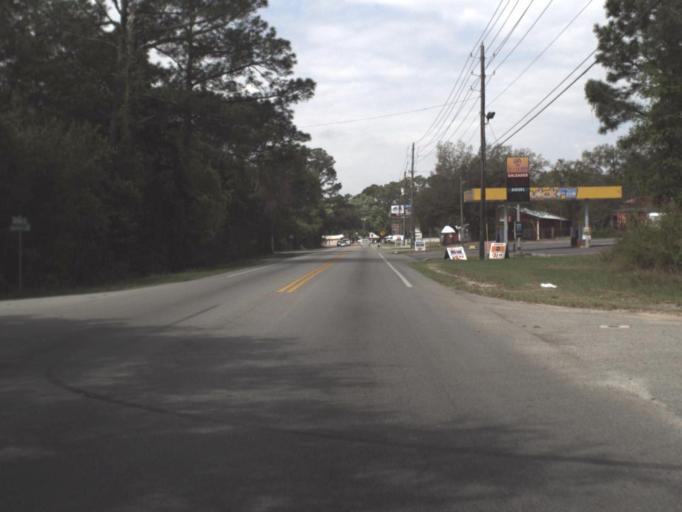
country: US
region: Florida
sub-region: Escambia County
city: Warrington
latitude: 30.3796
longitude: -87.3122
